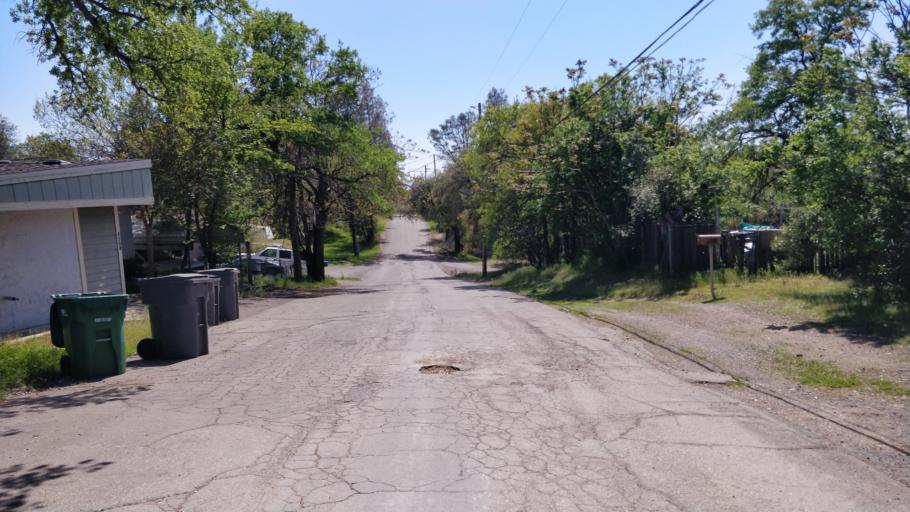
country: US
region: California
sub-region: Shasta County
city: Shasta Lake
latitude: 40.6680
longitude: -122.3559
